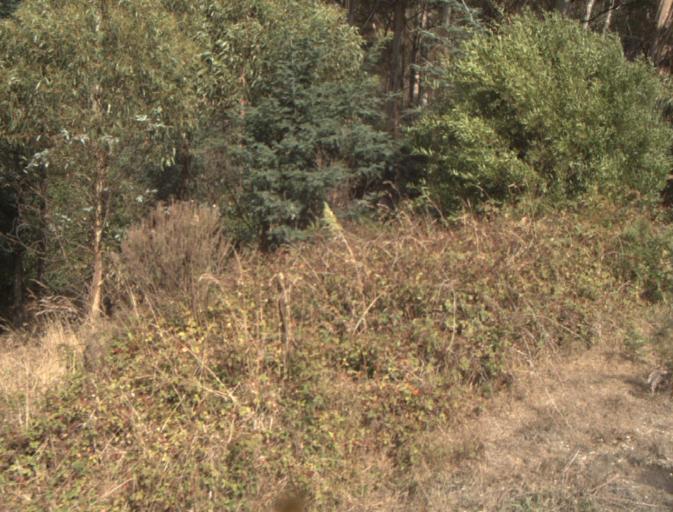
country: AU
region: Tasmania
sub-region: Launceston
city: Mayfield
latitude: -41.1829
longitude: 147.1939
